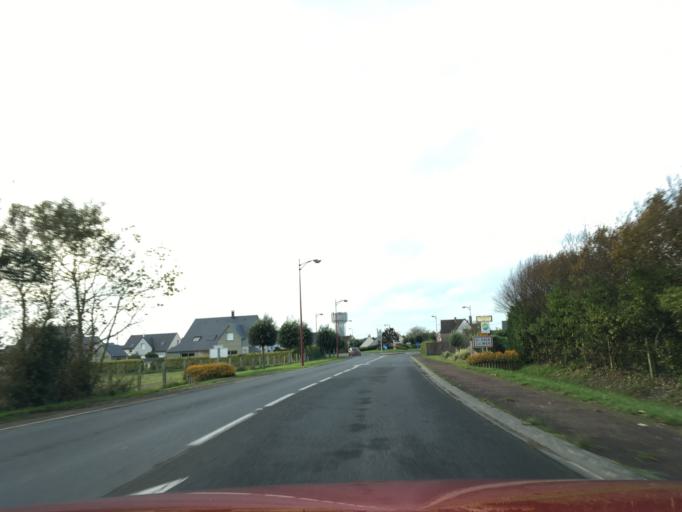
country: FR
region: Lower Normandy
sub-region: Departement de la Manche
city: Saint-Pair-sur-Mer
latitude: 48.8133
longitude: -1.5540
